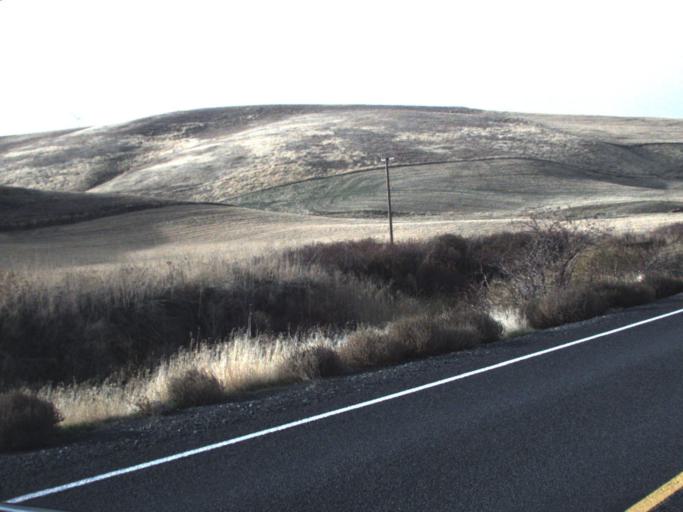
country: US
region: Washington
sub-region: Garfield County
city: Pomeroy
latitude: 46.4968
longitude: -117.7725
